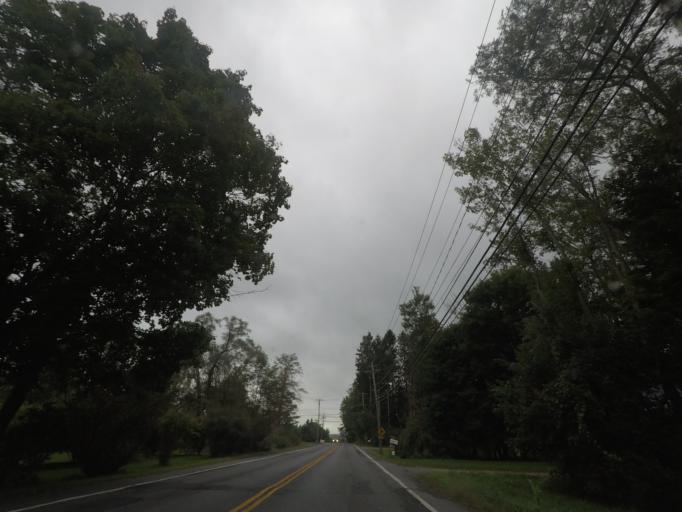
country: US
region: New York
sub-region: Rensselaer County
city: Hoosick Falls
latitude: 42.9209
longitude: -73.3491
